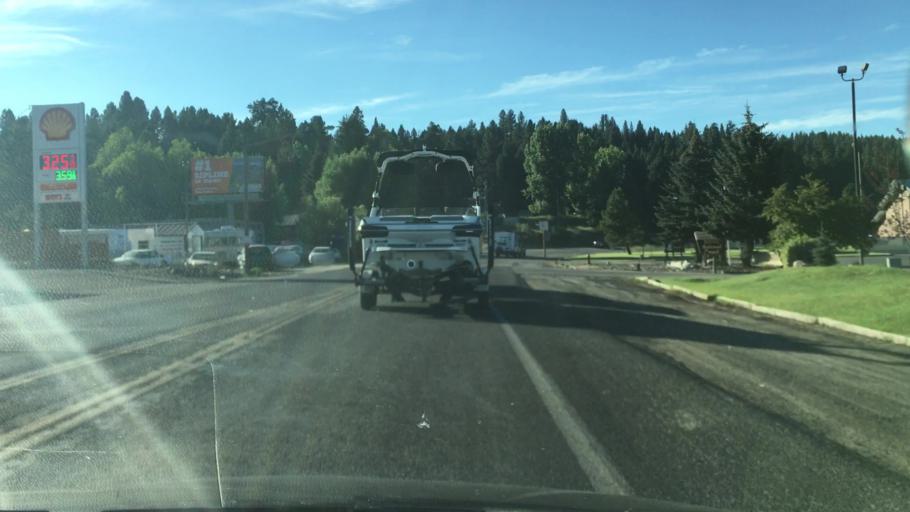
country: US
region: Idaho
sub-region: Valley County
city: Cascade
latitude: 44.5195
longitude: -116.0450
